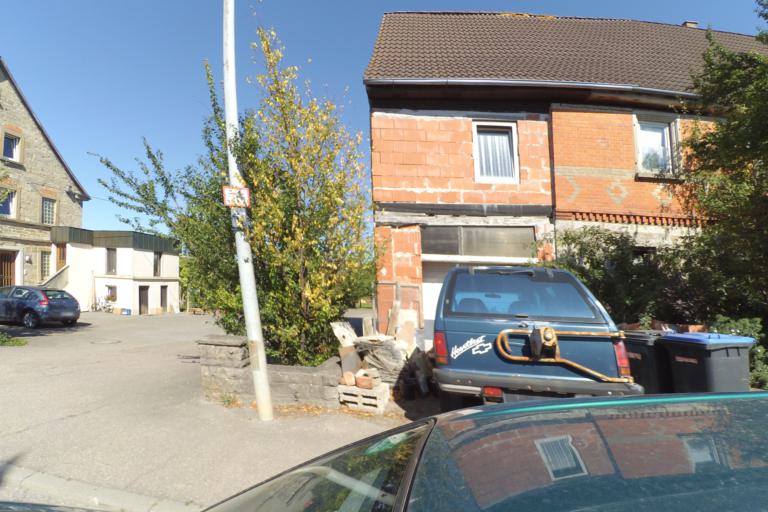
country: DE
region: Baden-Wuerttemberg
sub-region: Regierungsbezirk Stuttgart
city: Blaufelden
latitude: 49.2956
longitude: 9.9700
